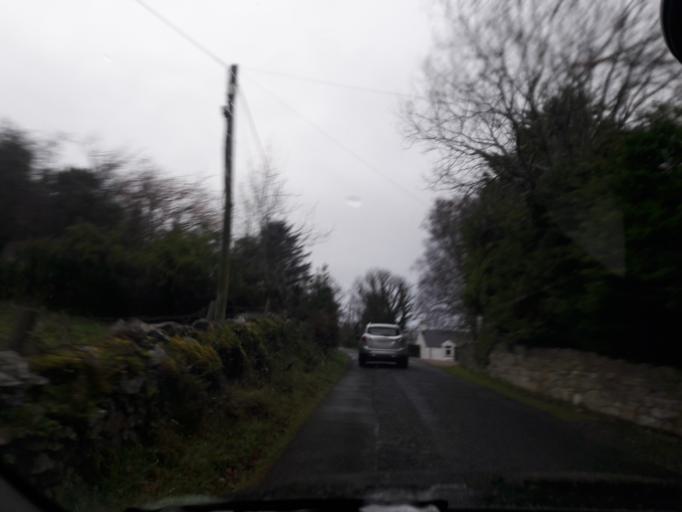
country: IE
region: Ulster
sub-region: County Donegal
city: Buncrana
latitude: 55.2219
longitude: -7.6115
